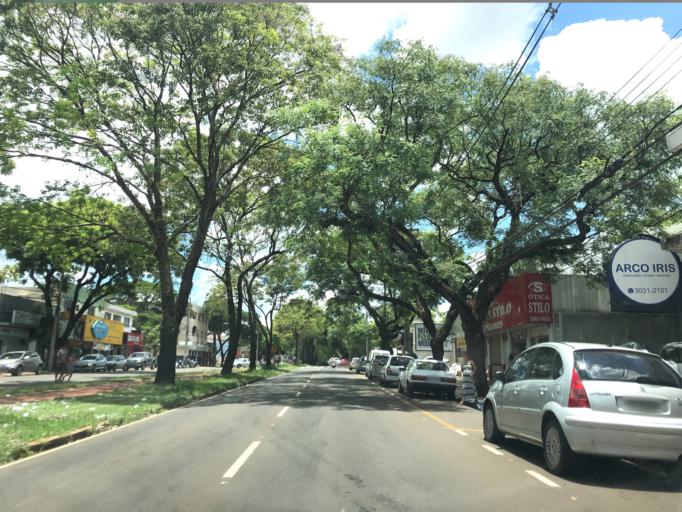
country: BR
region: Parana
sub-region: Maringa
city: Maringa
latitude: -23.4025
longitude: -51.9210
